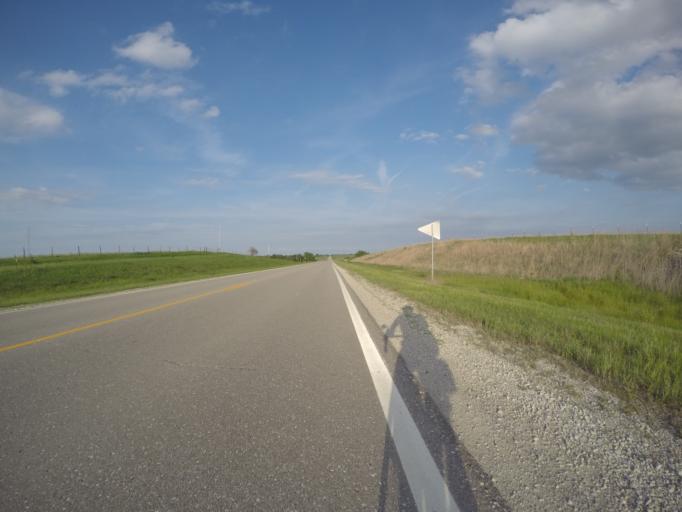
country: US
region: Kansas
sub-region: Pottawatomie County
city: Westmoreland
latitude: 39.4282
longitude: -96.6019
